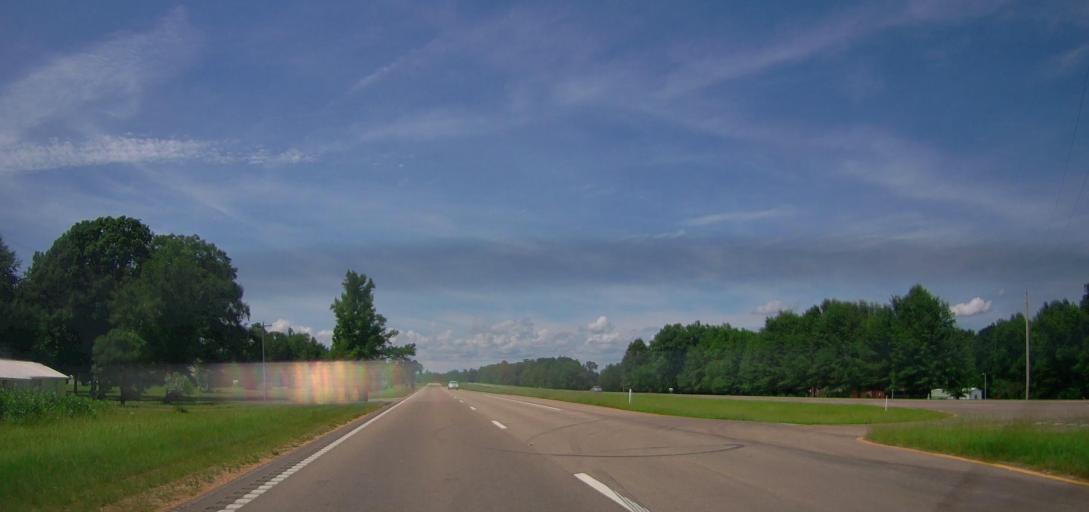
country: US
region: Mississippi
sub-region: Monroe County
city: Aberdeen
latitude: 33.9299
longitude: -88.5965
